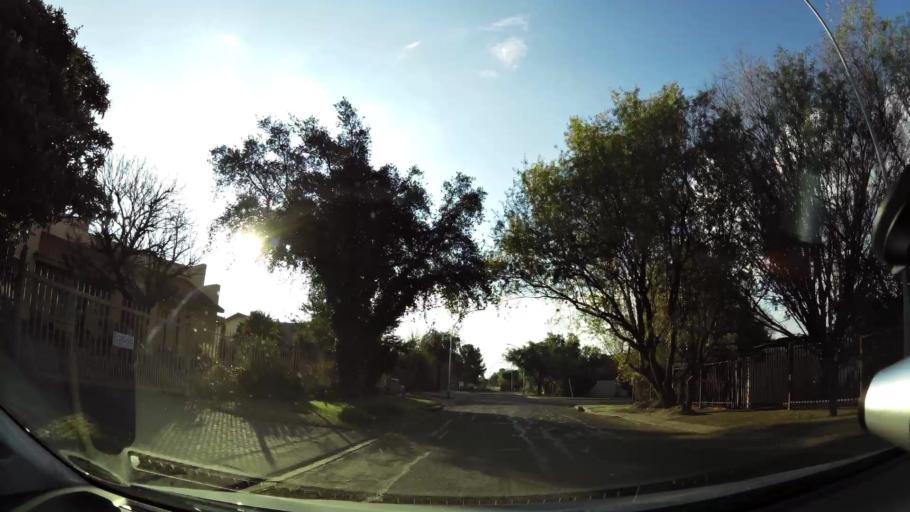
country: ZA
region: Orange Free State
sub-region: Mangaung Metropolitan Municipality
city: Bloemfontein
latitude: -29.1506
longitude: 26.1748
